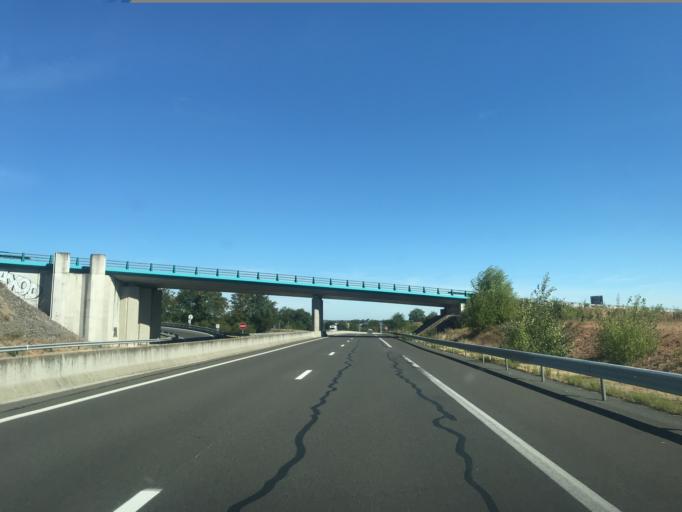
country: FR
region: Auvergne
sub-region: Departement de l'Allier
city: Premilhat
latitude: 46.3328
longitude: 2.5368
